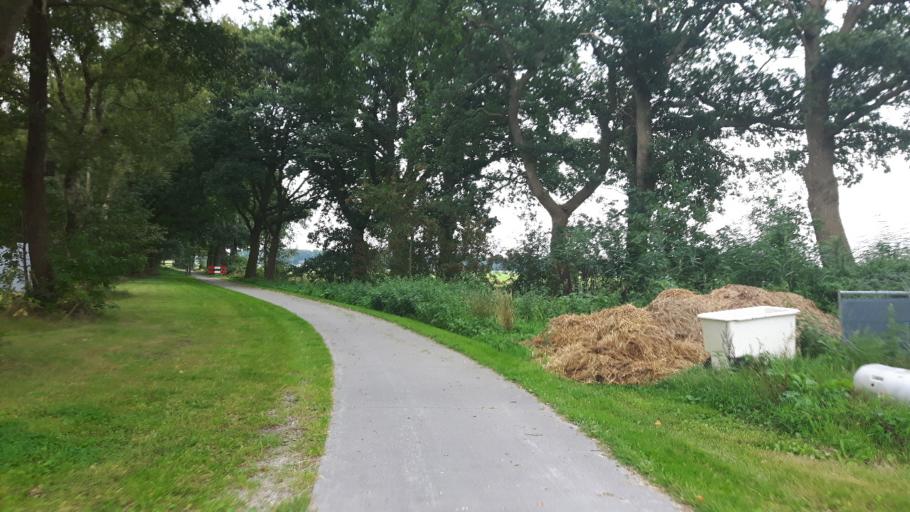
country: NL
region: Friesland
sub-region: Gemeente Weststellingwerf
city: Noordwolde
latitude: 52.9564
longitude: 6.2283
